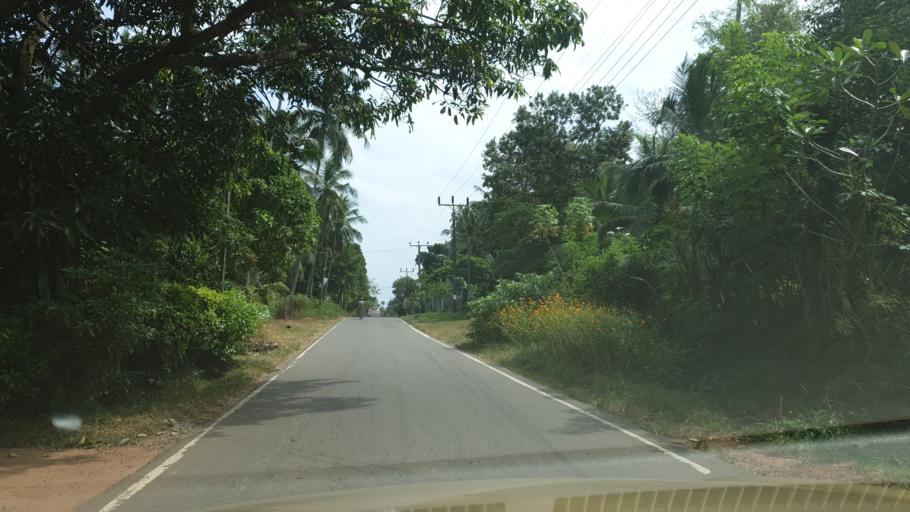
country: LK
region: North Western
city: Kuliyapitiya
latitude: 7.3477
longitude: 79.9813
